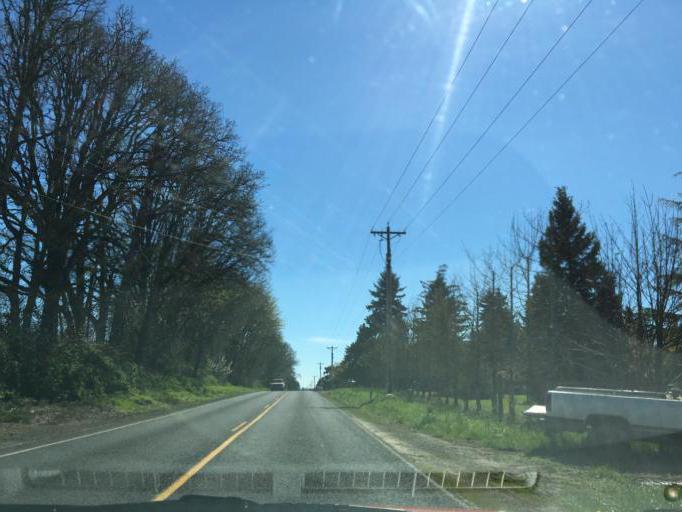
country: US
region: Oregon
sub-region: Marion County
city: Hubbard
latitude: 45.1693
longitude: -122.7226
